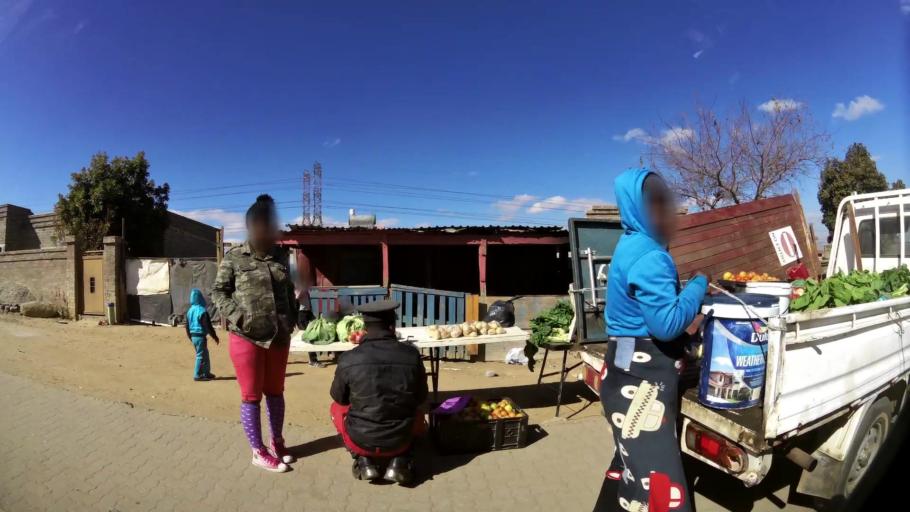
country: ZA
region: Gauteng
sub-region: City of Johannesburg Metropolitan Municipality
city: Modderfontein
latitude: -26.0346
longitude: 28.1624
